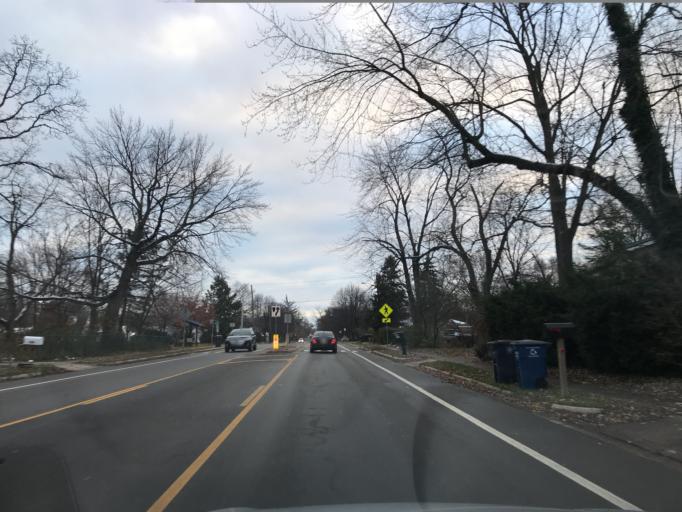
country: US
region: Michigan
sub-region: Washtenaw County
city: Ann Arbor
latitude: 42.2431
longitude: -83.7001
